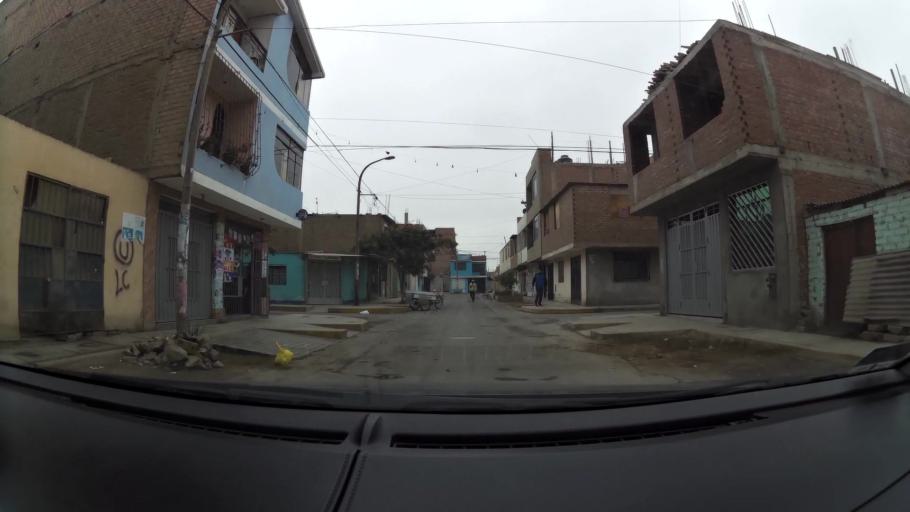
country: PE
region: Lima
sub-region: Lima
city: Independencia
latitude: -11.9660
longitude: -77.0755
